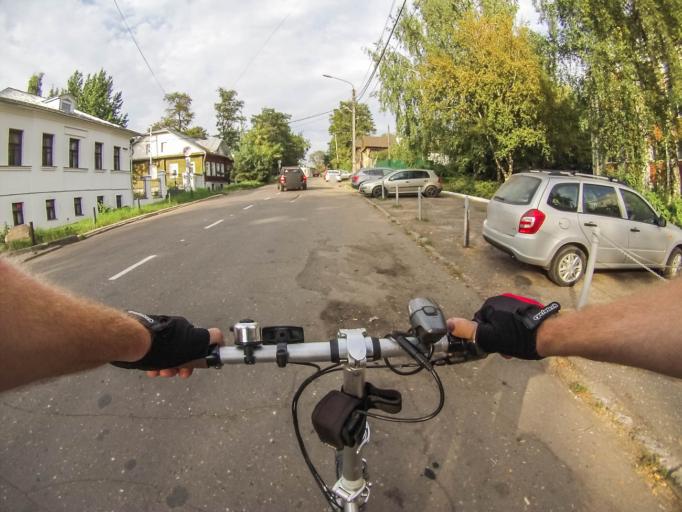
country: RU
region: Kostroma
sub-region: Kostromskoy Rayon
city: Kostroma
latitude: 57.7703
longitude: 40.9133
